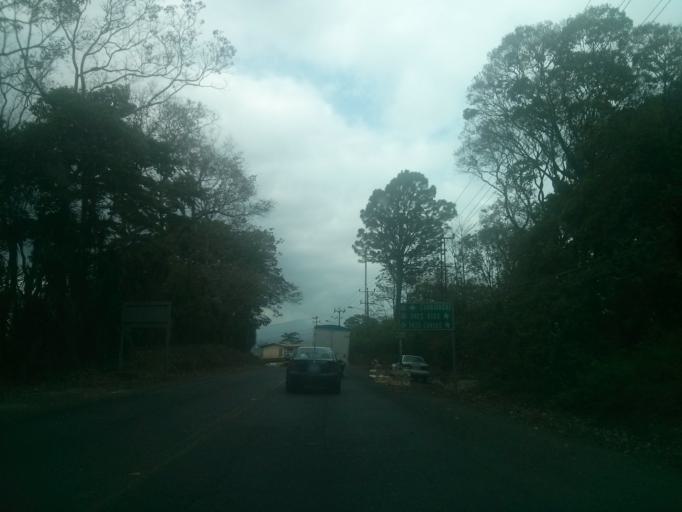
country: CR
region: San Jose
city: Curridabat
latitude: 9.9098
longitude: -84.0374
